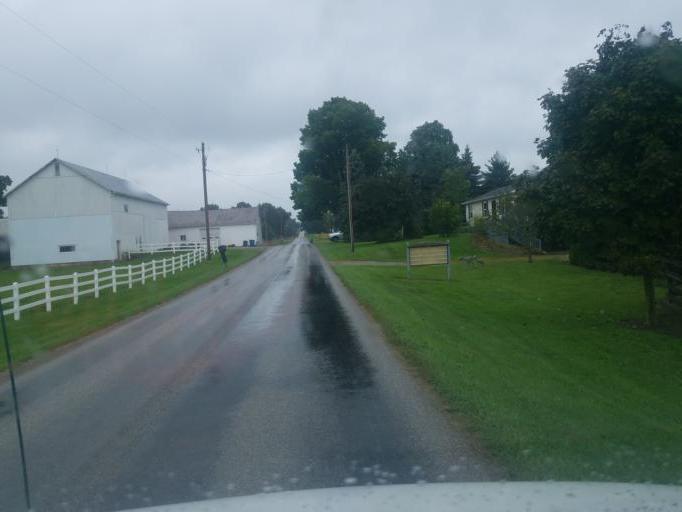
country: US
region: Ohio
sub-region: Wayne County
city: Creston
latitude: 40.9748
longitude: -81.9125
